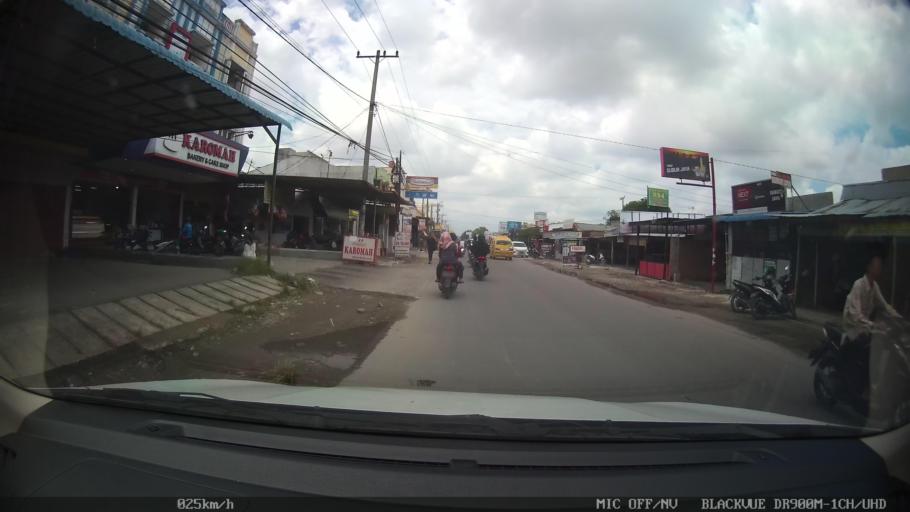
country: ID
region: North Sumatra
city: Medan
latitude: 3.6207
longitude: 98.7303
